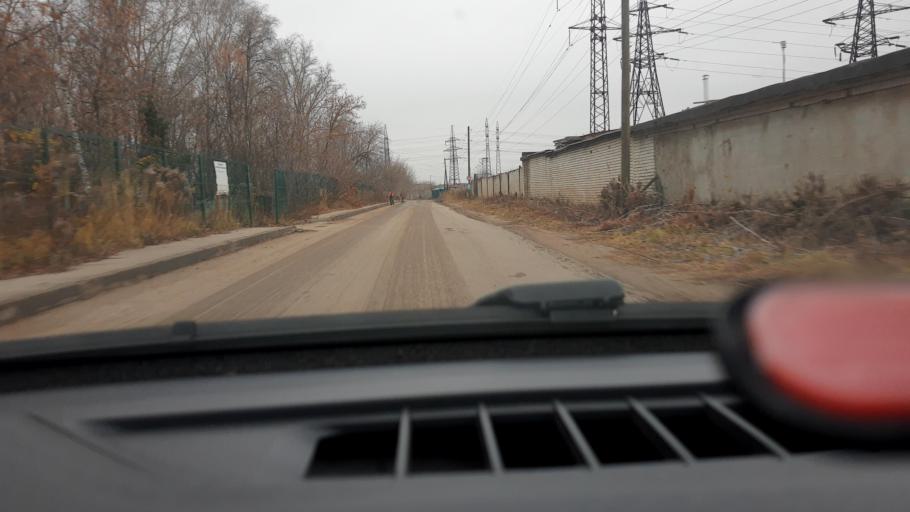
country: RU
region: Nizjnij Novgorod
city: Nizhniy Novgorod
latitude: 56.2862
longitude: 43.8810
